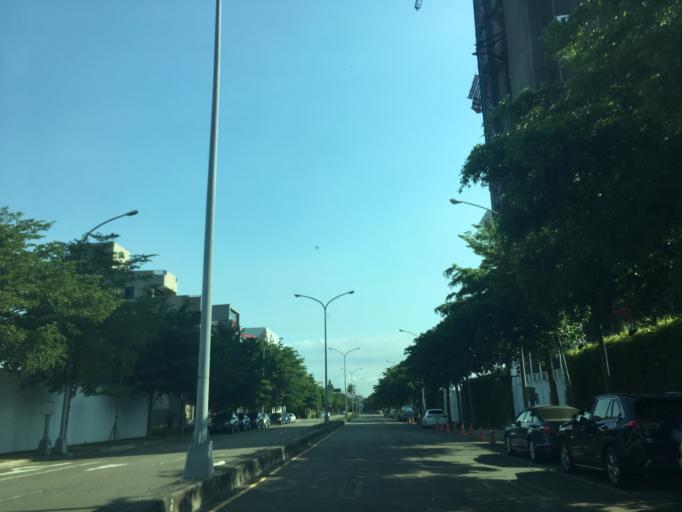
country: TW
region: Taiwan
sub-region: Taichung City
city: Taichung
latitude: 24.1576
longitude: 120.6288
